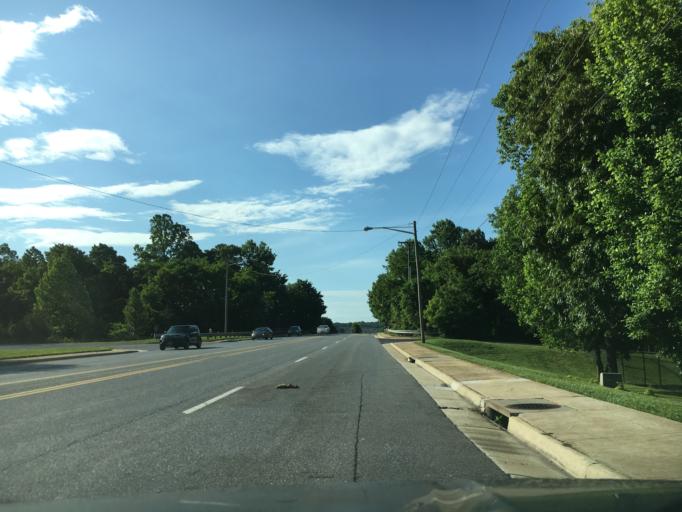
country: US
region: Virginia
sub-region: Bedford County
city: Forest
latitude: 37.3651
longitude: -79.2485
